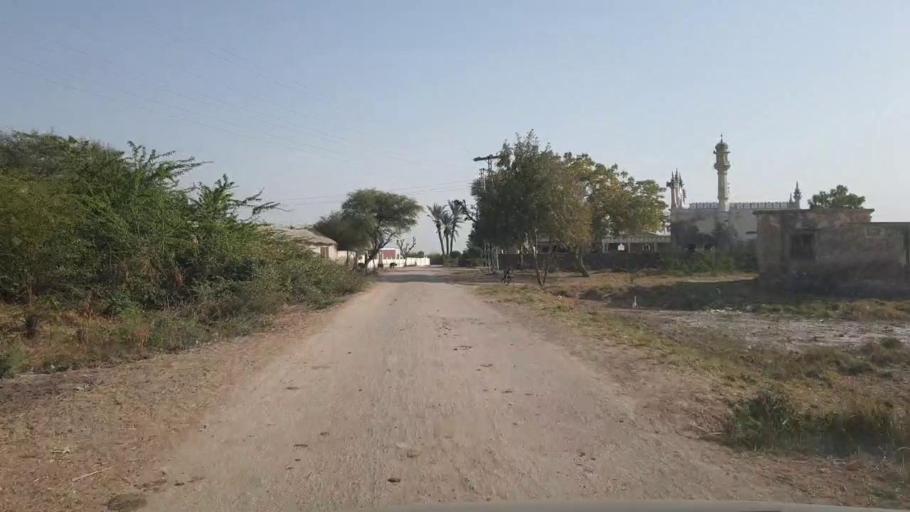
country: PK
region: Sindh
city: Dhoro Naro
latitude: 25.4647
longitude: 69.5511
